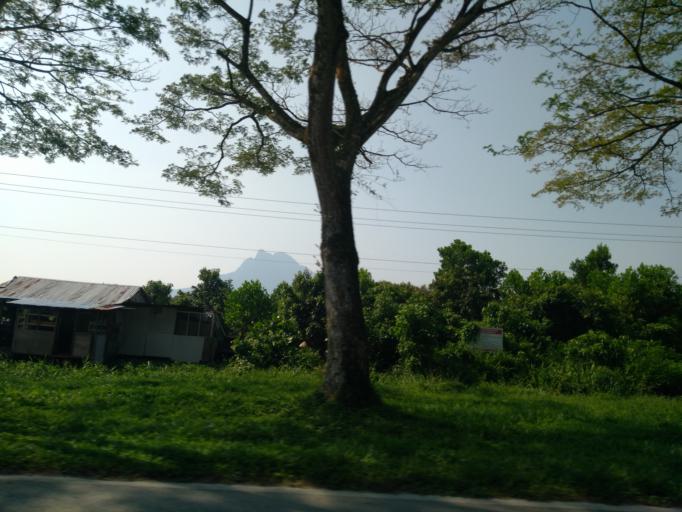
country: MY
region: Sarawak
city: Kuching
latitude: 1.6800
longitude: 110.3454
